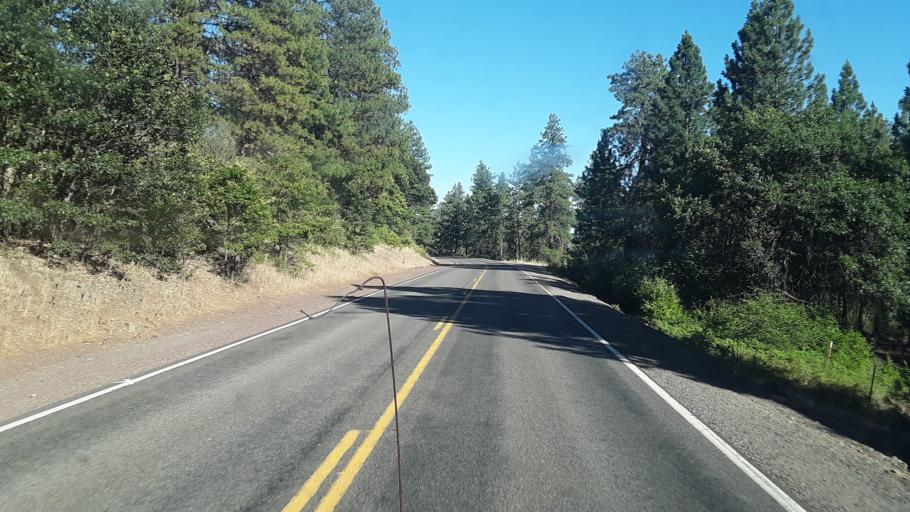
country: US
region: Oregon
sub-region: Klamath County
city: Klamath Falls
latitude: 42.2776
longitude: -121.9104
